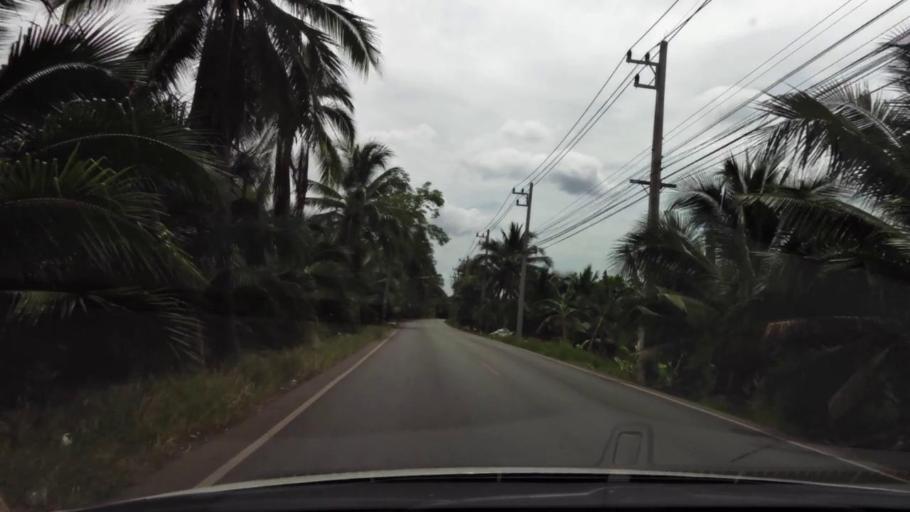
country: TH
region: Ratchaburi
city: Damnoen Saduak
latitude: 13.5383
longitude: 99.9993
